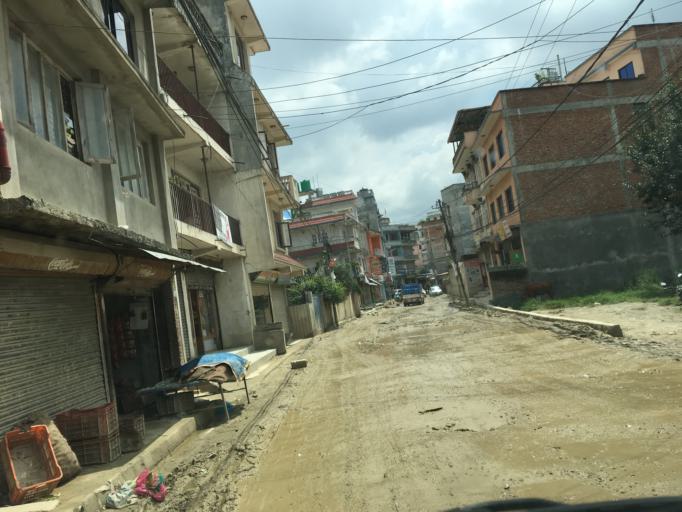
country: NP
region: Central Region
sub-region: Bagmati Zone
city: Kathmandu
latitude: 27.7232
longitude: 85.3493
